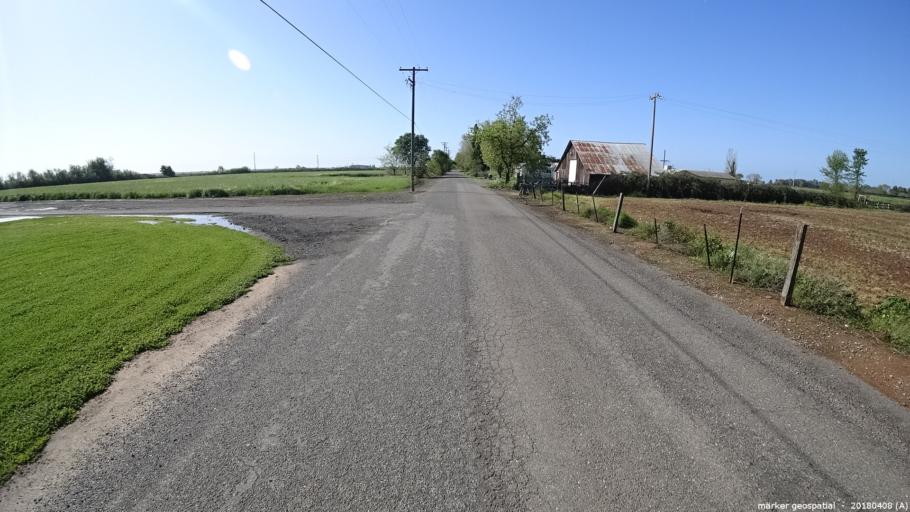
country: US
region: California
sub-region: Sacramento County
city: Elk Grove
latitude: 38.3646
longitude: -121.4037
